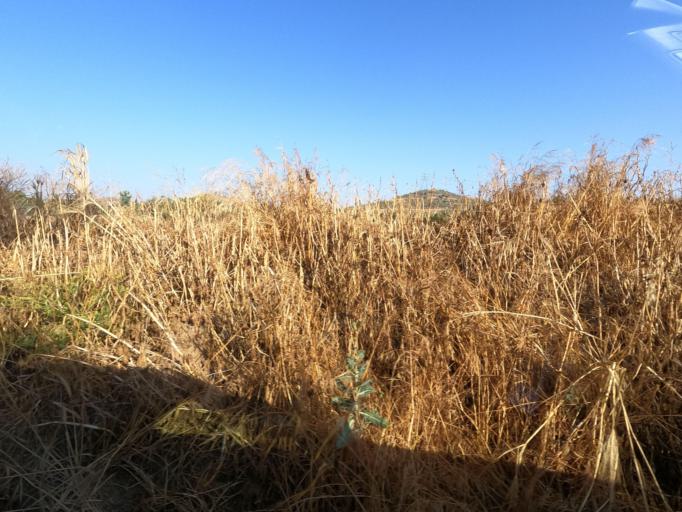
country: CY
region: Lefkosia
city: Lympia
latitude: 34.9823
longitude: 33.4382
